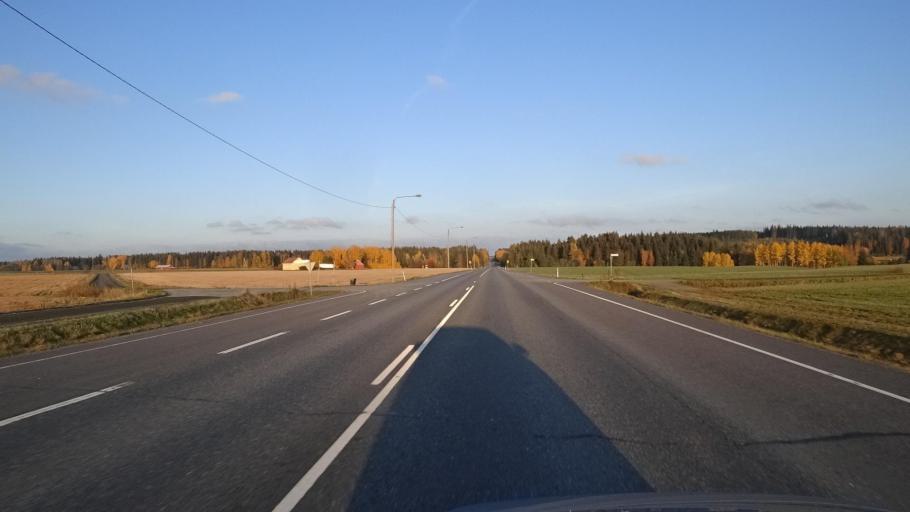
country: FI
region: Haeme
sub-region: Forssa
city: Jokioinen
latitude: 60.7840
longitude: 23.4495
